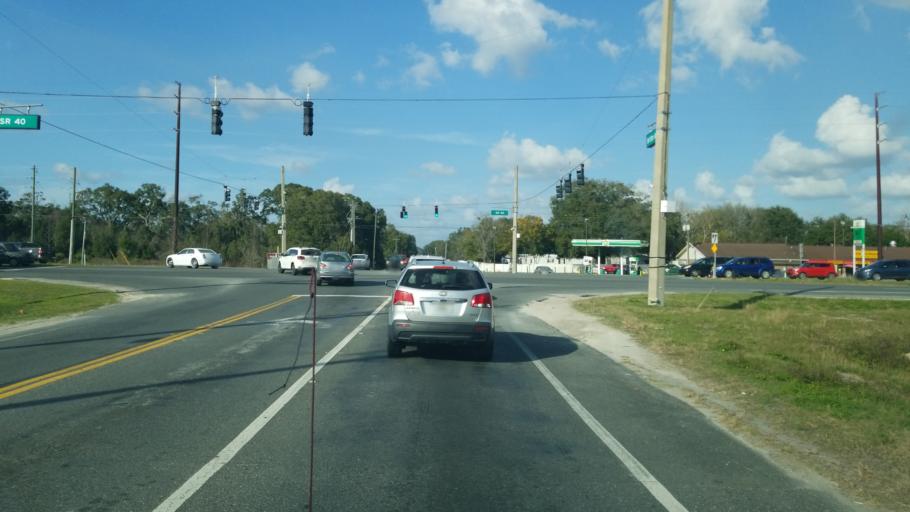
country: US
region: Florida
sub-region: Marion County
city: Ocala
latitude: 29.1861
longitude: -82.2516
